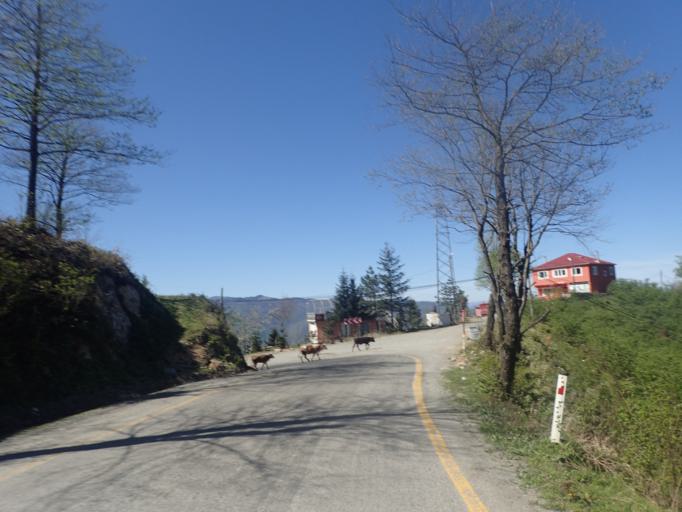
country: TR
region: Ordu
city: Kabaduz
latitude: 40.8052
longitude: 37.9071
